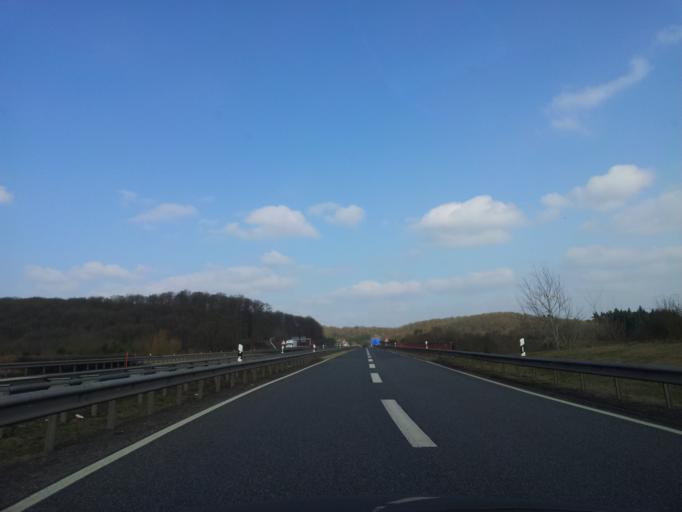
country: DE
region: Rheinland-Pfalz
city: Altrich
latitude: 49.9472
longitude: 6.8831
